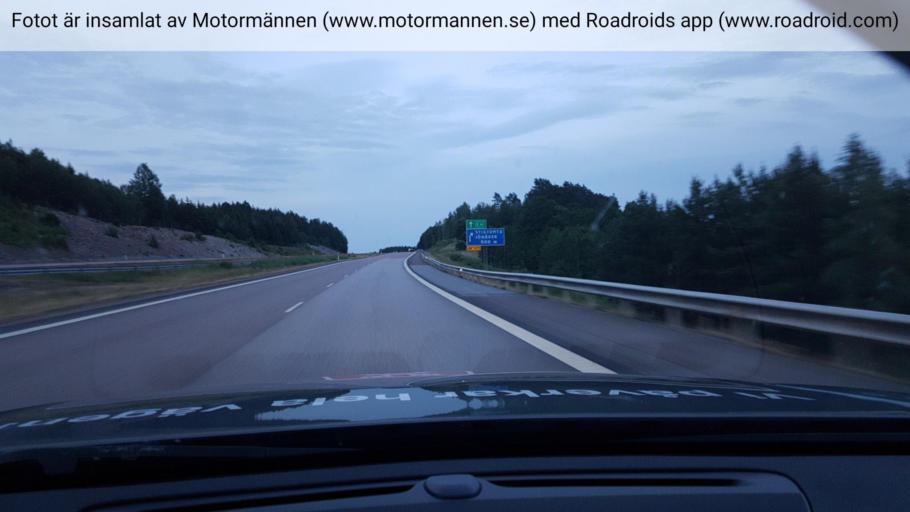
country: SE
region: Soedermanland
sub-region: Nykopings Kommun
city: Stigtomta
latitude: 58.7584
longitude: 16.7134
